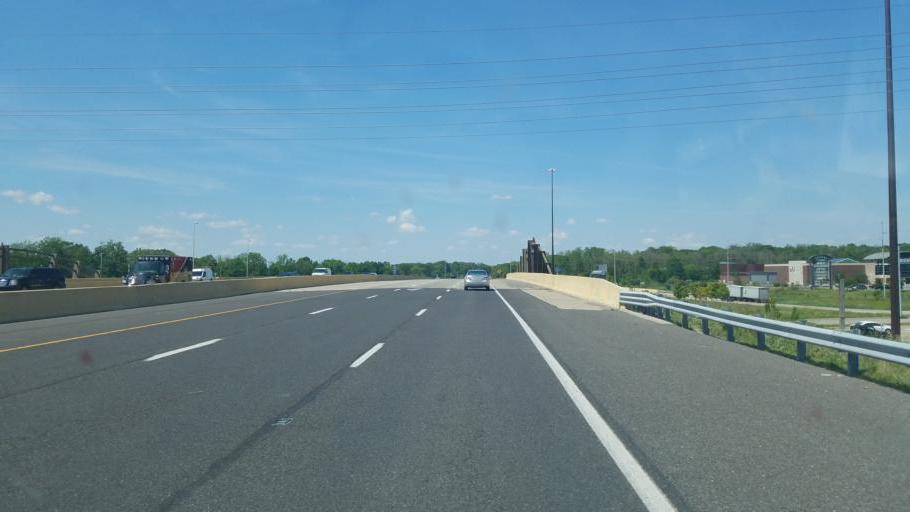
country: US
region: Indiana
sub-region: Boone County
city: Zionsville
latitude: 39.9097
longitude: -86.2695
